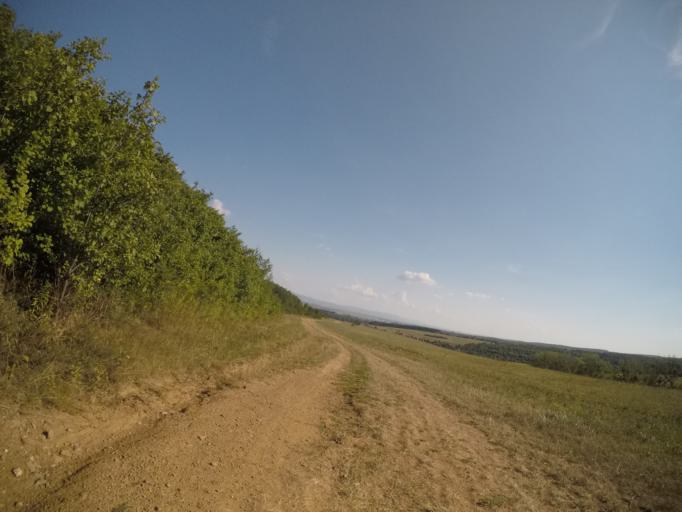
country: SK
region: Kosicky
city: Kosice
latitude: 48.7374
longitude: 21.2102
